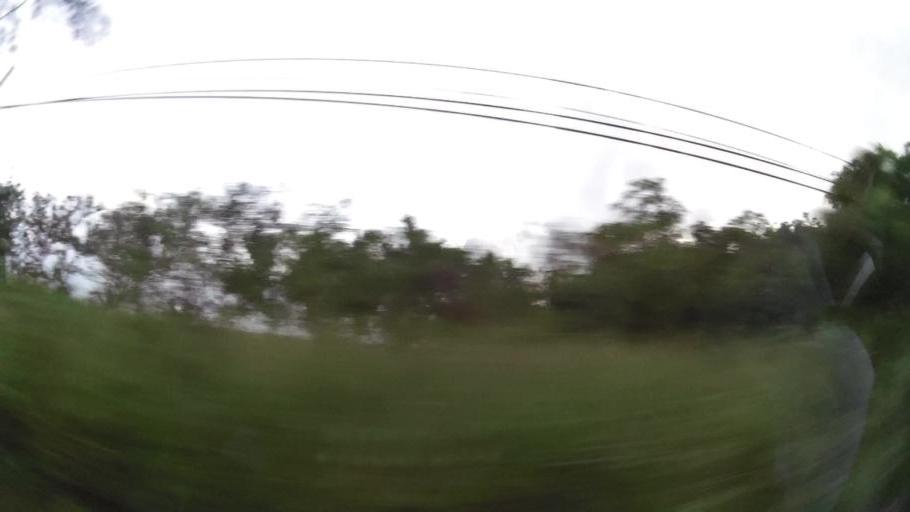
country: BB
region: Saint Philip
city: Crane
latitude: 13.1186
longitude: -59.4943
